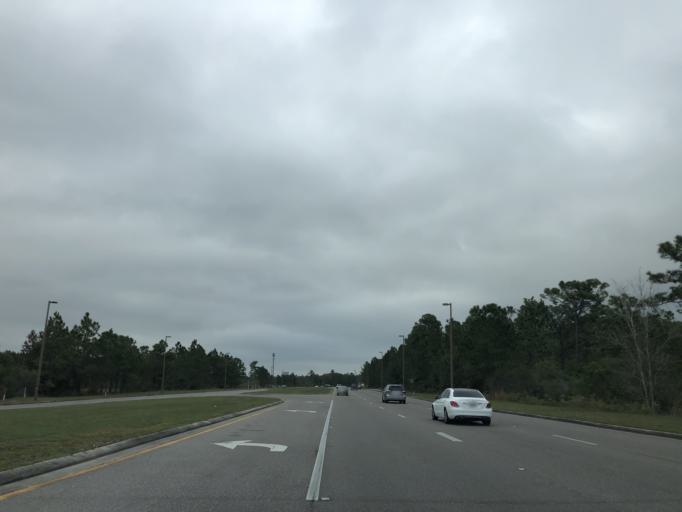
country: US
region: Florida
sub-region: Osceola County
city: Celebration
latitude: 28.3472
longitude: -81.5221
